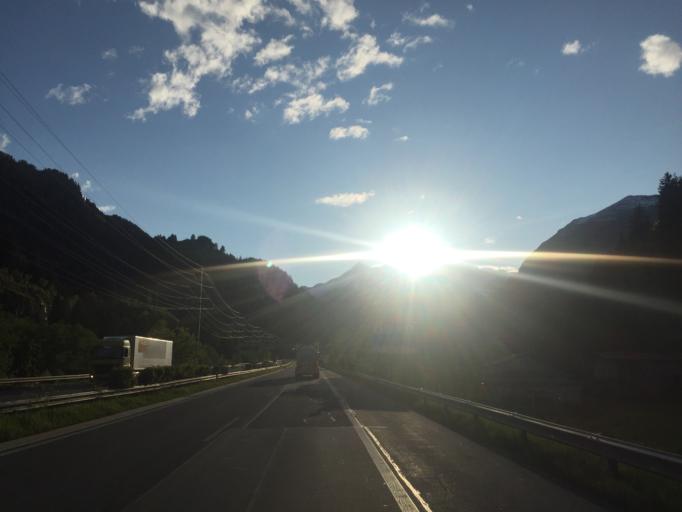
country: CH
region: Ticino
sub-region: Leventina District
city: Airolo
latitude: 46.5194
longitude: 8.6460
